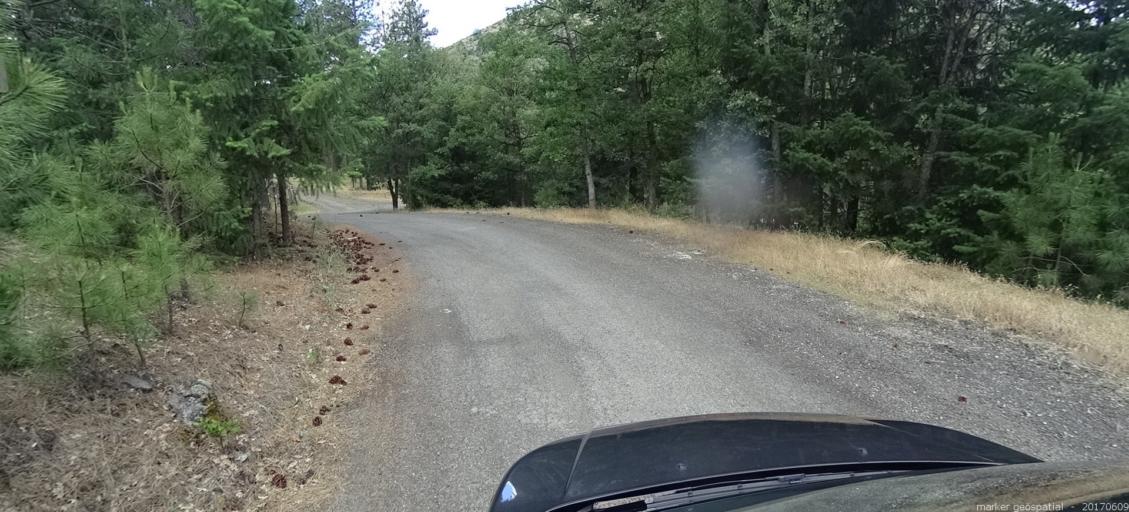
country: US
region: California
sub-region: Siskiyou County
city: Weed
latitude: 41.3008
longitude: -122.7994
